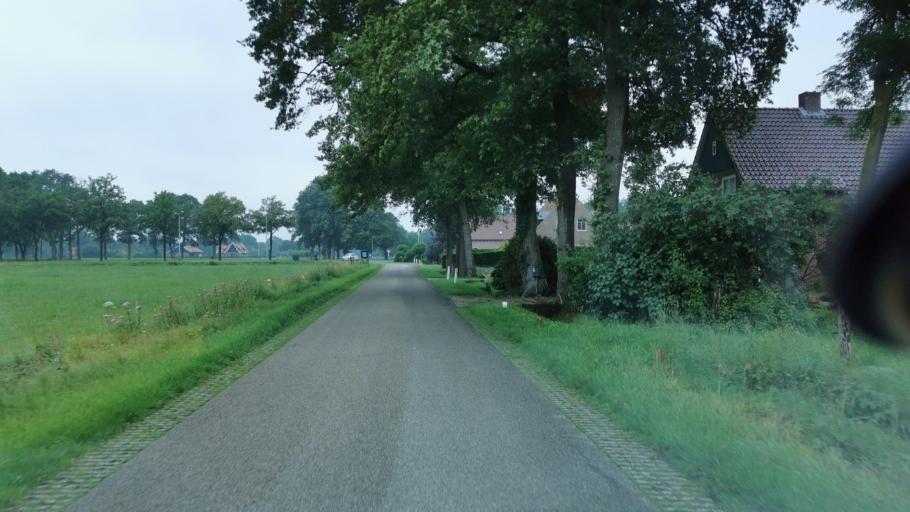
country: NL
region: Overijssel
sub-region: Gemeente Losser
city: Losser
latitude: 52.2719
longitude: 6.9865
